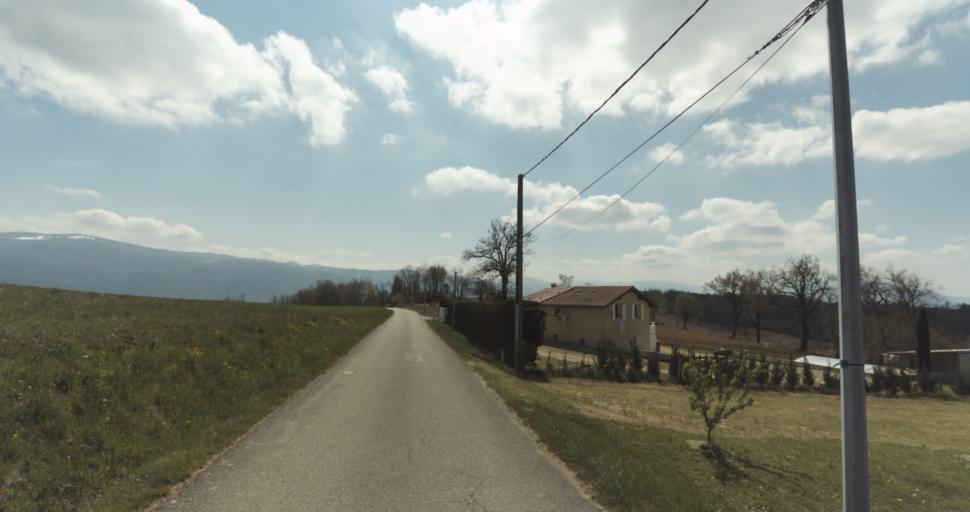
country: FR
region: Rhone-Alpes
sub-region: Departement de l'Isere
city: Saint-Verand
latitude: 45.1713
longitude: 5.3074
